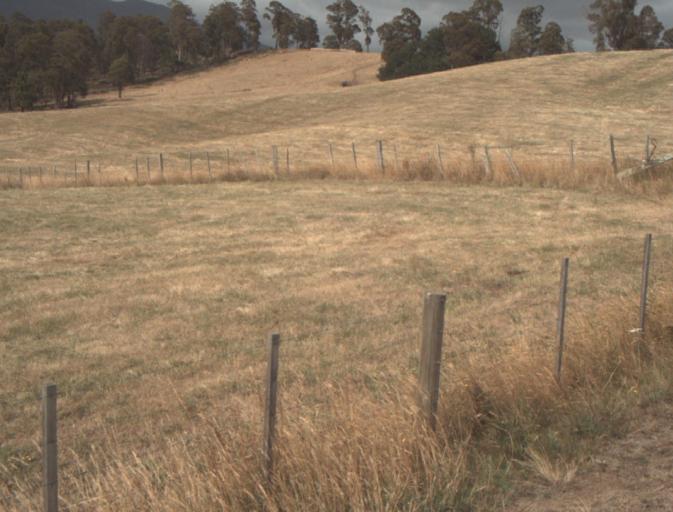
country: AU
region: Tasmania
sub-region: Dorset
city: Scottsdale
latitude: -41.4545
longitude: 147.6010
